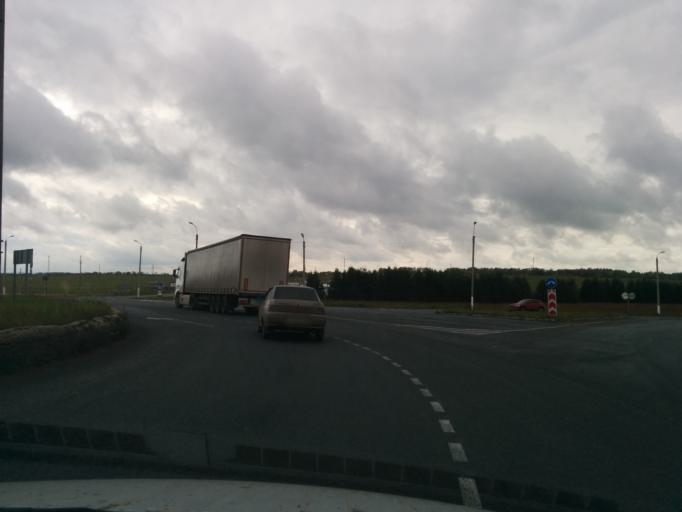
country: RU
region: Tatarstan
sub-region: Bavlinskiy Rayon
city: Bavly
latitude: 54.4229
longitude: 53.1578
